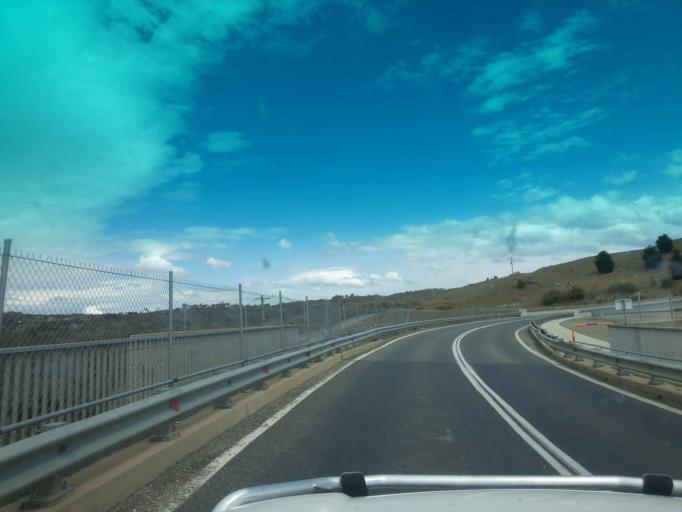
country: AU
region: New South Wales
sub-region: Snowy River
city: Jindabyne
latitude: -36.4347
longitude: 148.6325
